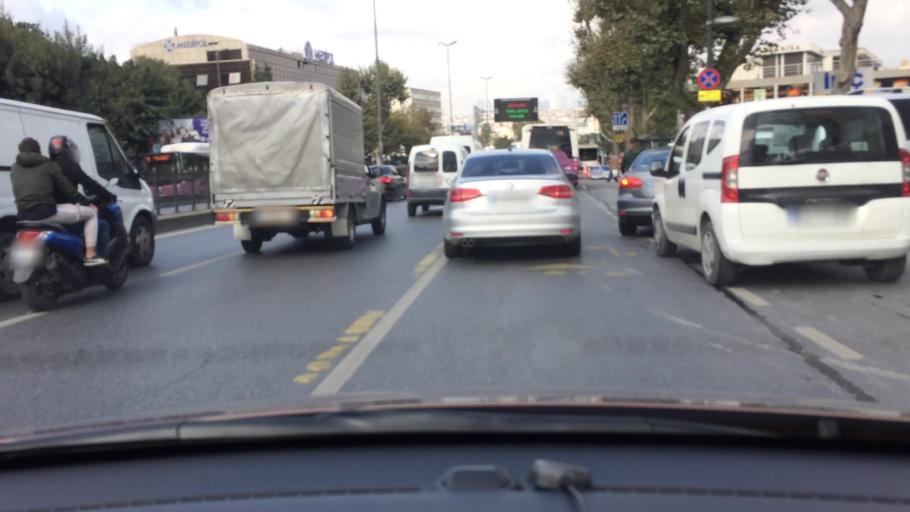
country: TR
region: Istanbul
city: Istanbul
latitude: 41.0201
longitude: 28.9590
